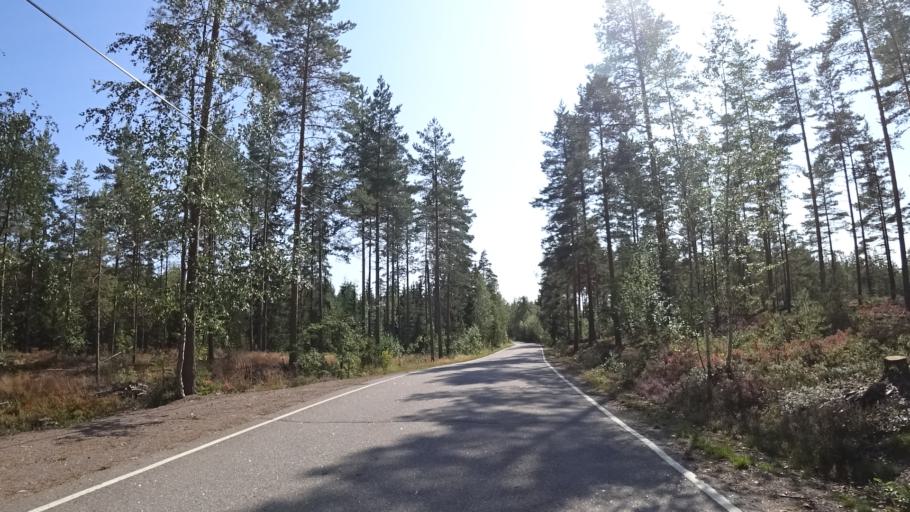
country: FI
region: Kymenlaakso
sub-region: Kotka-Hamina
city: Karhula
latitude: 60.5618
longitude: 26.9012
